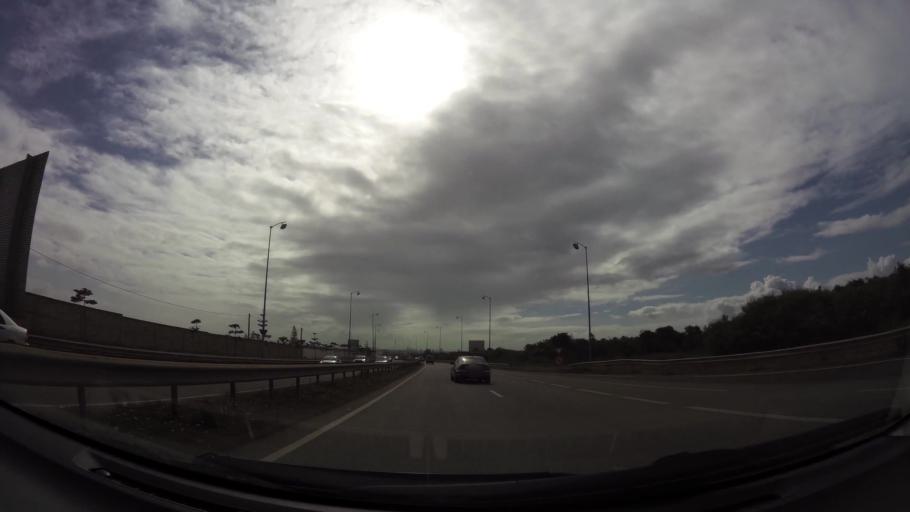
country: MA
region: Doukkala-Abda
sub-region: El-Jadida
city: El Jadida
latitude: 33.2465
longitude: -8.4560
